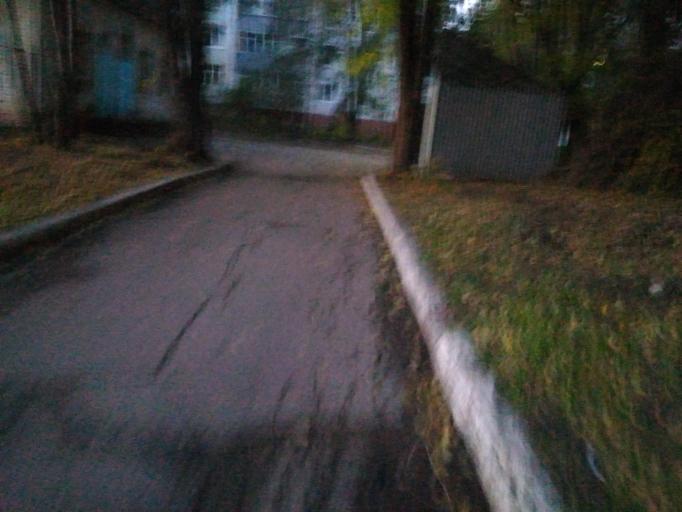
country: RU
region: Ulyanovsk
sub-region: Ulyanovskiy Rayon
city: Ulyanovsk
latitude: 54.3307
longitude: 48.3917
